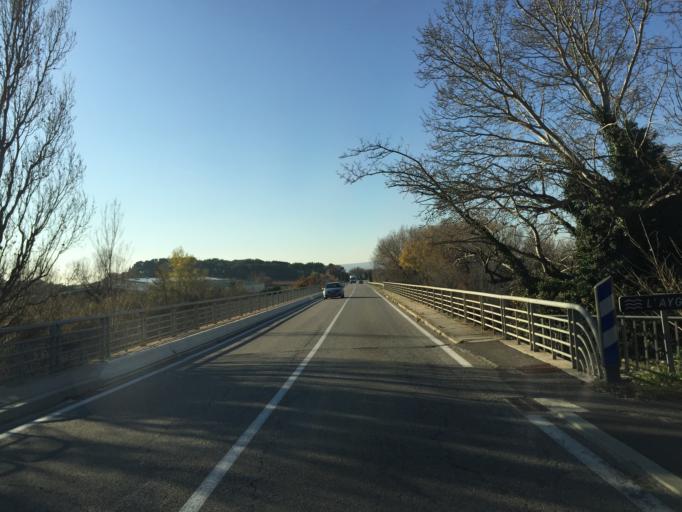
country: FR
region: Provence-Alpes-Cote d'Azur
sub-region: Departement du Vaucluse
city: Sainte-Cecile-les-Vignes
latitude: 44.2300
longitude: 4.9230
